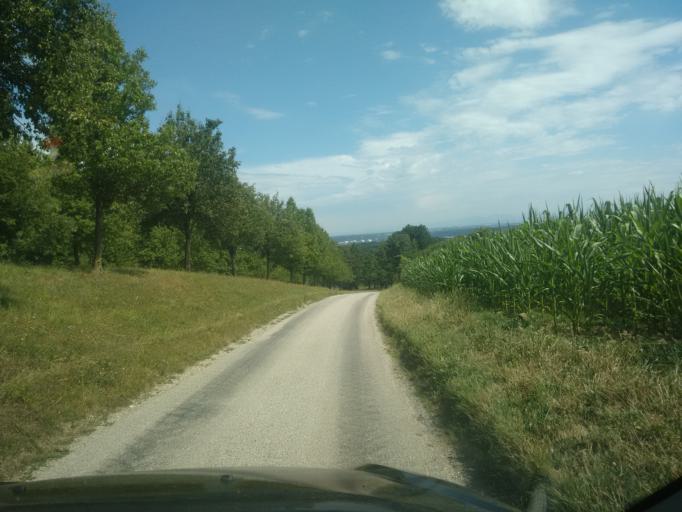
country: AT
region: Upper Austria
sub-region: Wels-Land
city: Gunskirchen
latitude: 48.1722
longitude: 13.9323
